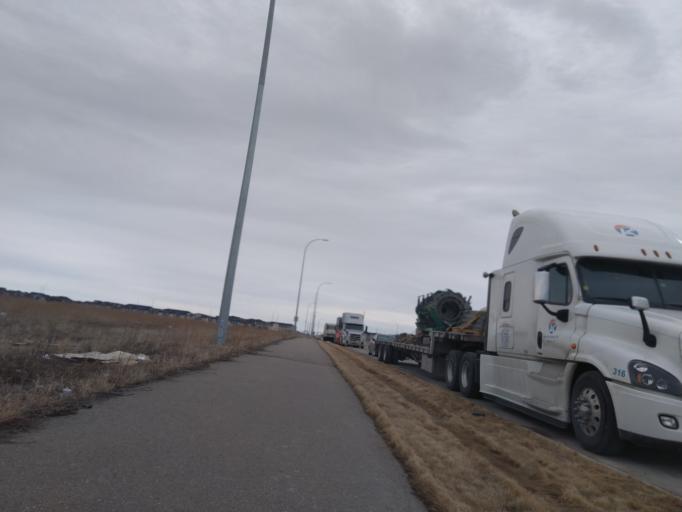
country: CA
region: Alberta
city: Airdrie
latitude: 51.1656
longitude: -113.9751
